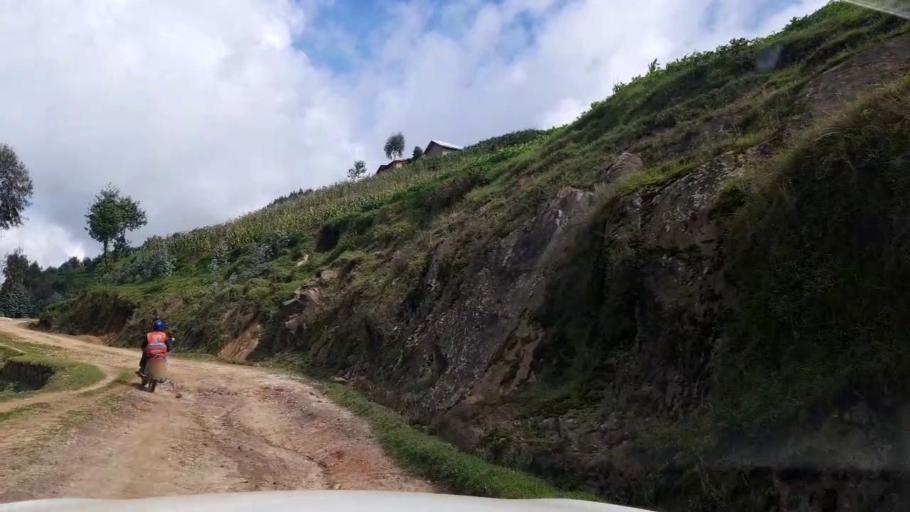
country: RW
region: Western Province
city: Kibuye
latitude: -1.8799
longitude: 29.4744
